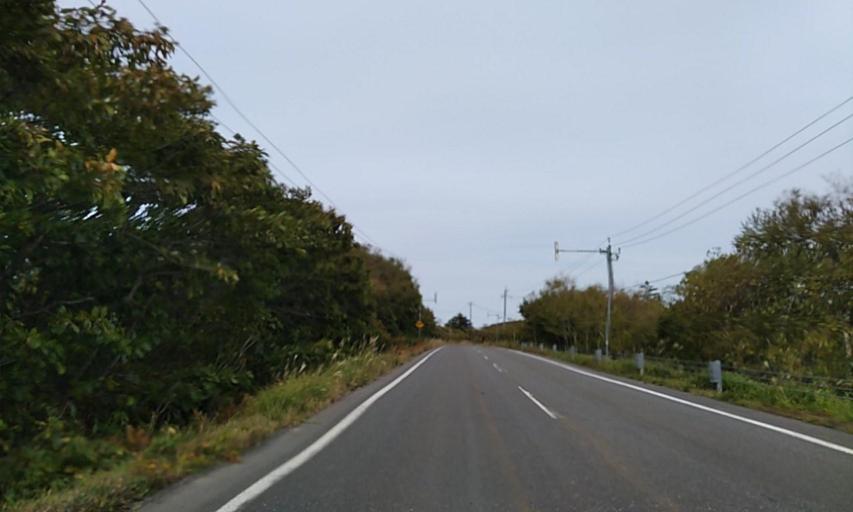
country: JP
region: Hokkaido
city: Makubetsu
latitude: 45.0023
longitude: 141.6998
